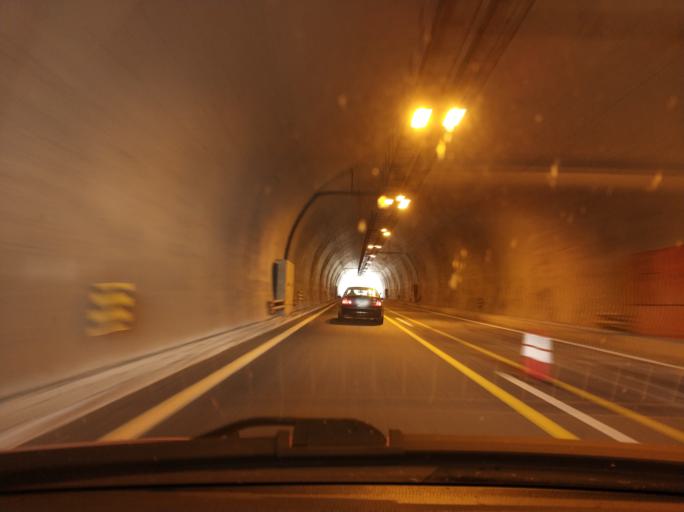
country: GR
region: East Macedonia and Thrace
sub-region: Nomos Kavalas
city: Palaio Tsifliki
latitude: 40.9060
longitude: 24.3419
